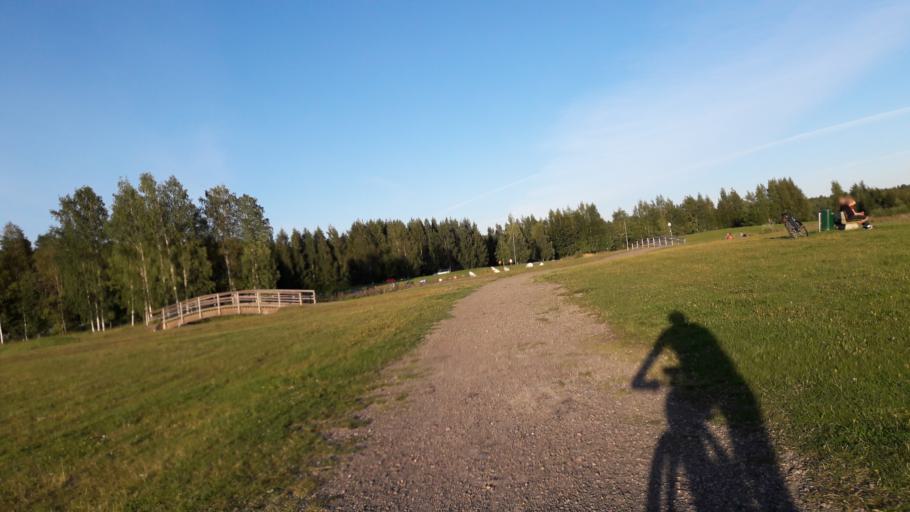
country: FI
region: North Karelia
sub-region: Joensuu
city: Joensuu
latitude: 62.6128
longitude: 29.7046
